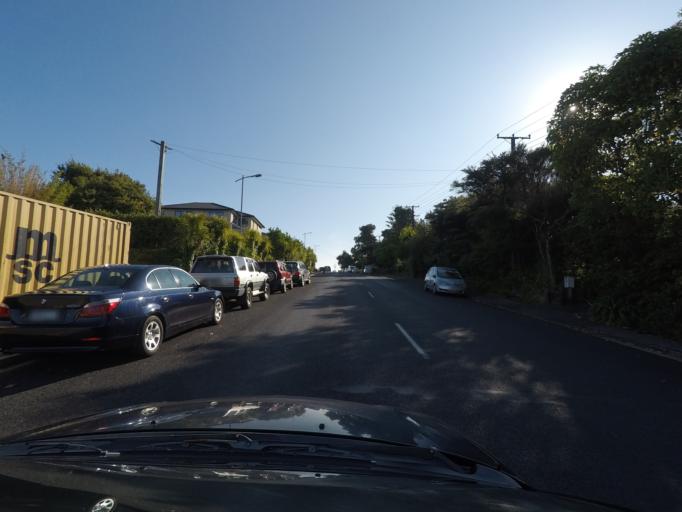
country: NZ
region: Auckland
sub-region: Auckland
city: Rosebank
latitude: -36.8724
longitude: 174.6012
